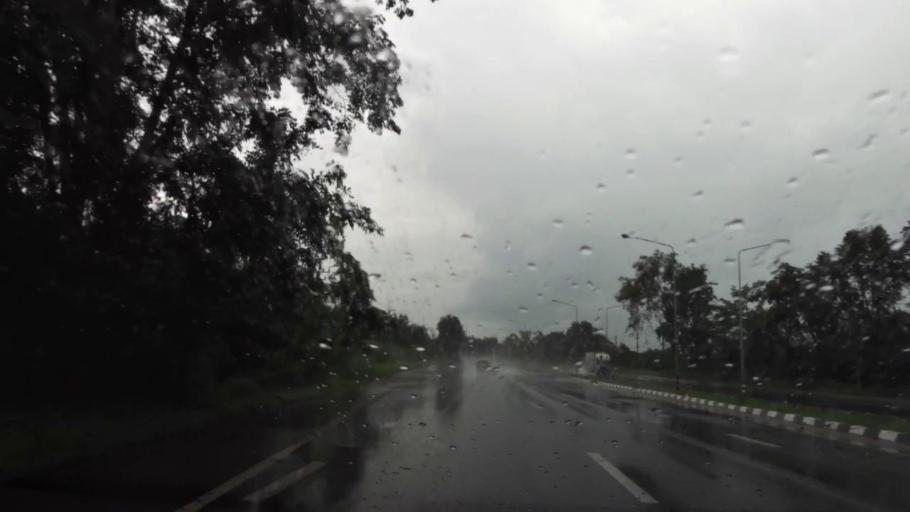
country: TH
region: Chon Buri
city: Nong Yai
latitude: 13.0527
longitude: 101.4283
